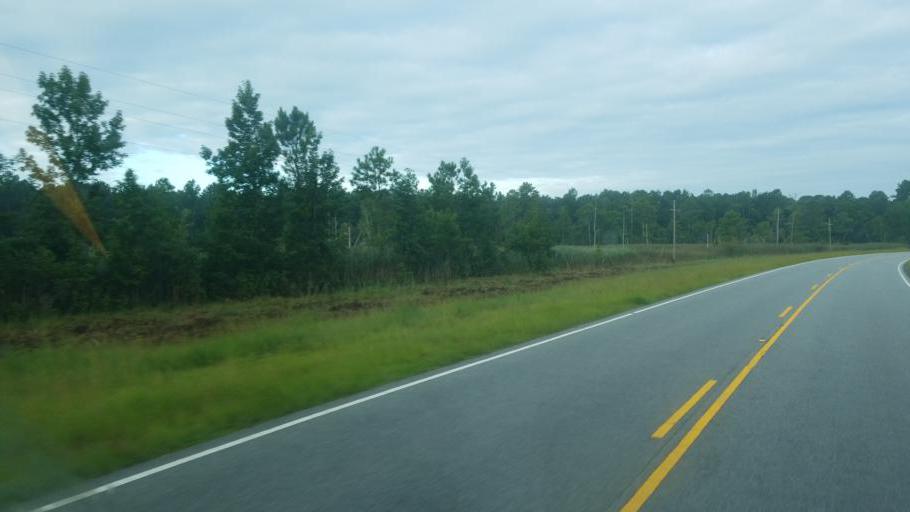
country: US
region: North Carolina
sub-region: Dare County
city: Manteo
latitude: 35.8638
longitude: -75.8564
